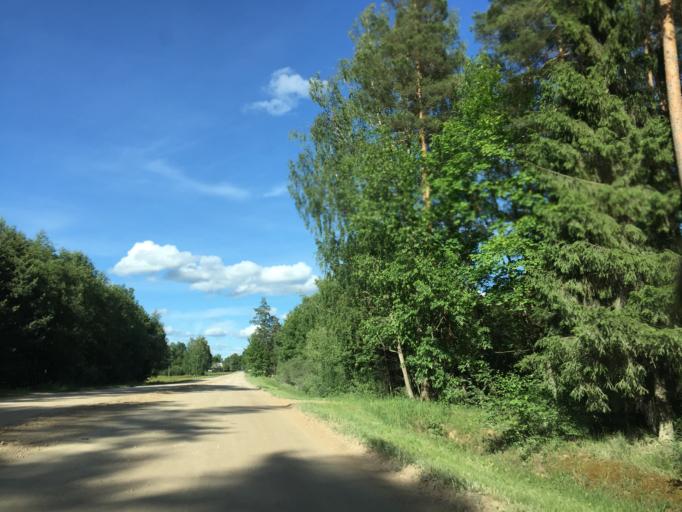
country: LV
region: Vecumnieki
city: Vecumnieki
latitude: 56.4484
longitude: 24.5862
